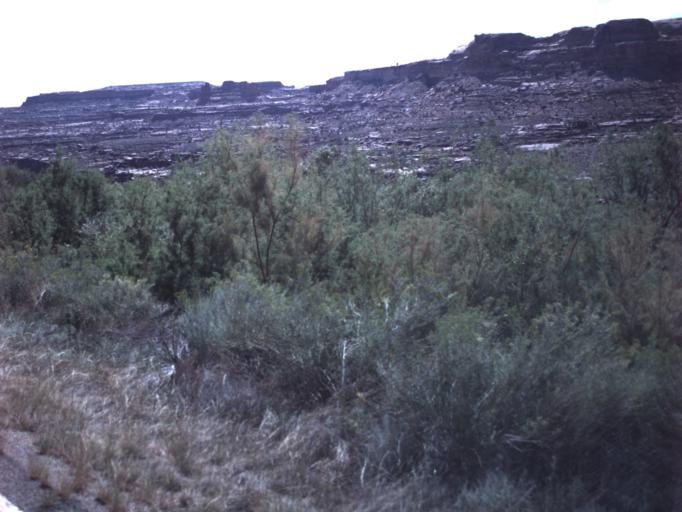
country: US
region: Utah
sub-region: Grand County
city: Moab
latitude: 38.5538
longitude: -109.6311
